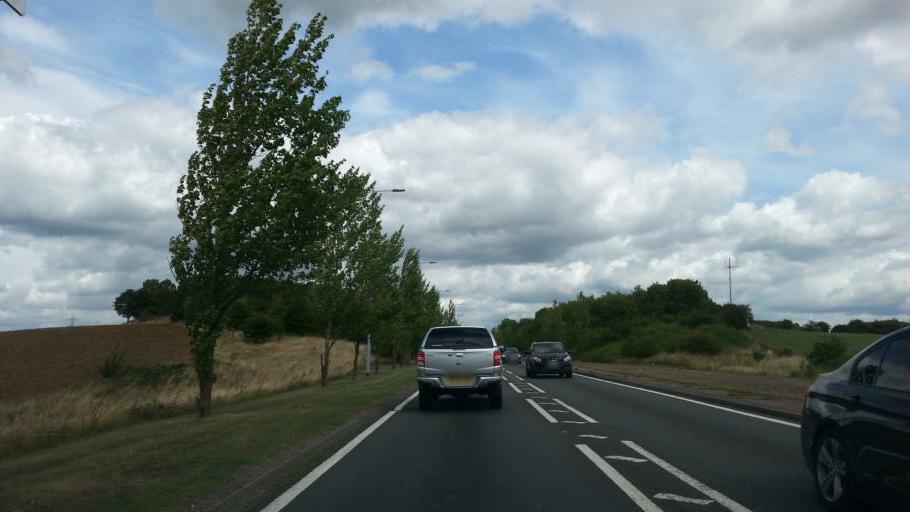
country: GB
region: England
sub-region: Essex
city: South Benfleet
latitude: 51.5585
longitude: 0.5399
